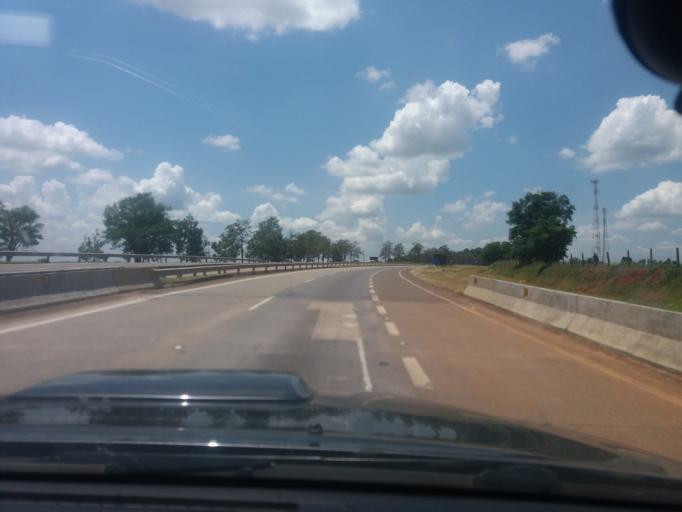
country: BR
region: Sao Paulo
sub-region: Itapetininga
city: Itapetininga
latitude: -23.4921
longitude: -47.9683
